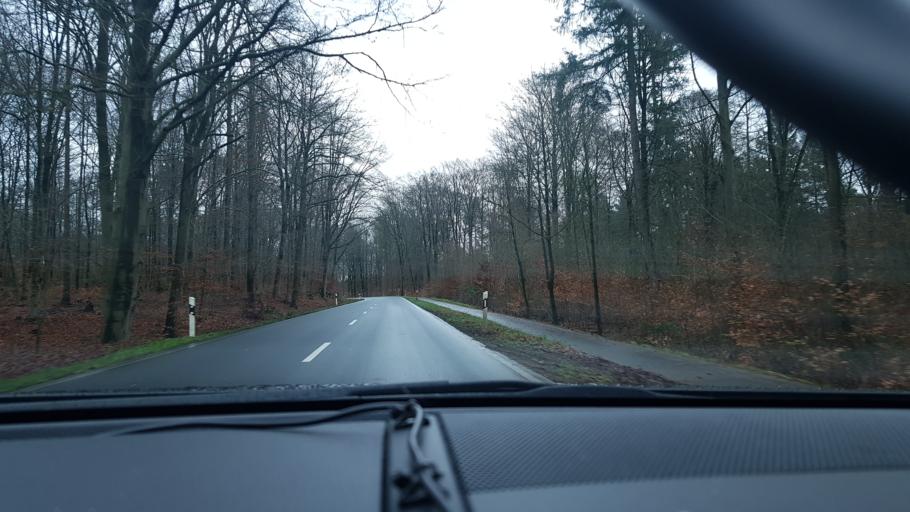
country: NL
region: Limburg
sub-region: Gemeente Beesel
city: Offenbeek
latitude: 51.2302
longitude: 6.0832
